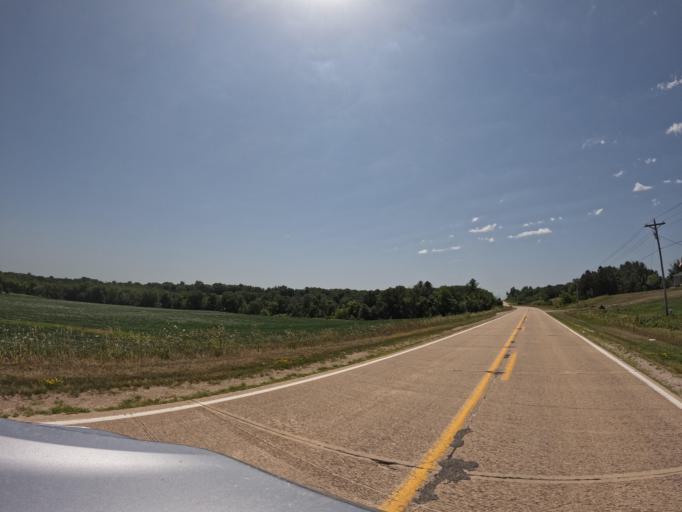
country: US
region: Iowa
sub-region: Henry County
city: Mount Pleasant
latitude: 40.9197
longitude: -91.5540
